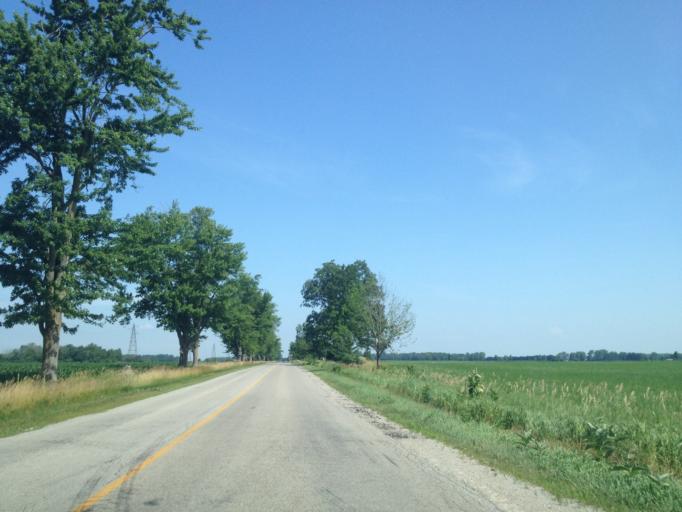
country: CA
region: Ontario
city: London
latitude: 43.0869
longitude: -81.2165
